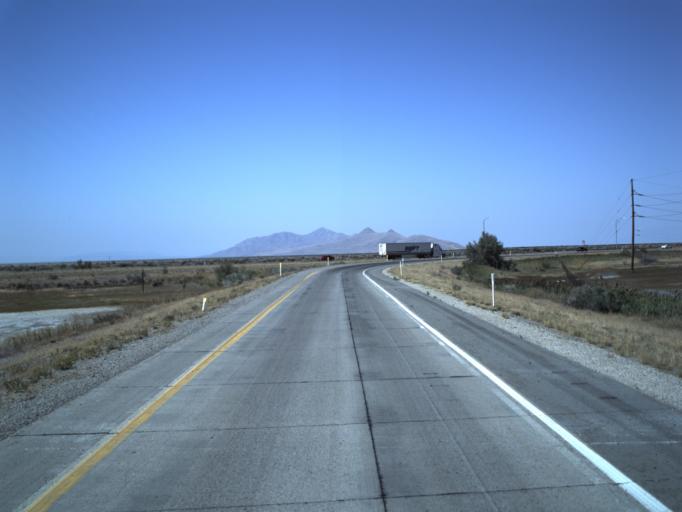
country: US
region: Utah
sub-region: Salt Lake County
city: Magna
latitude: 40.7461
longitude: -112.1792
